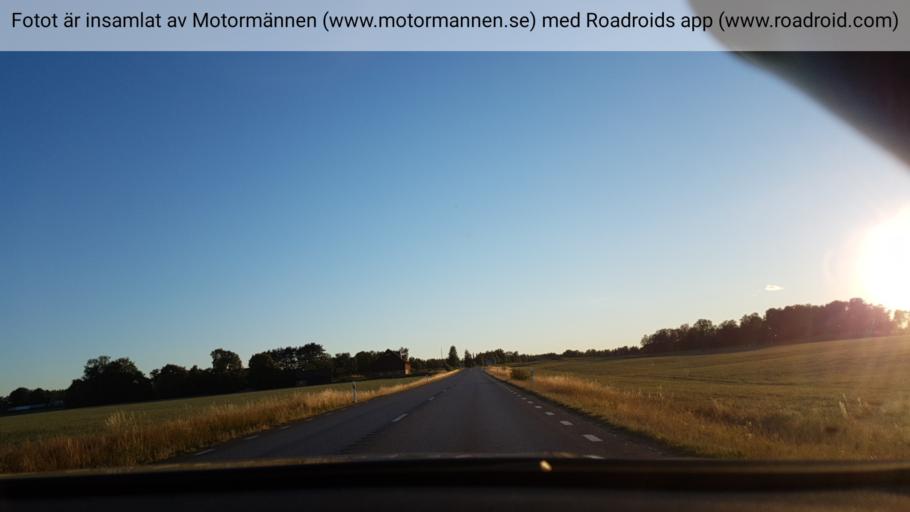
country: SE
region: Vaestra Goetaland
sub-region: Tidaholms Kommun
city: Olofstorp
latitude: 58.3527
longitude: 14.0641
